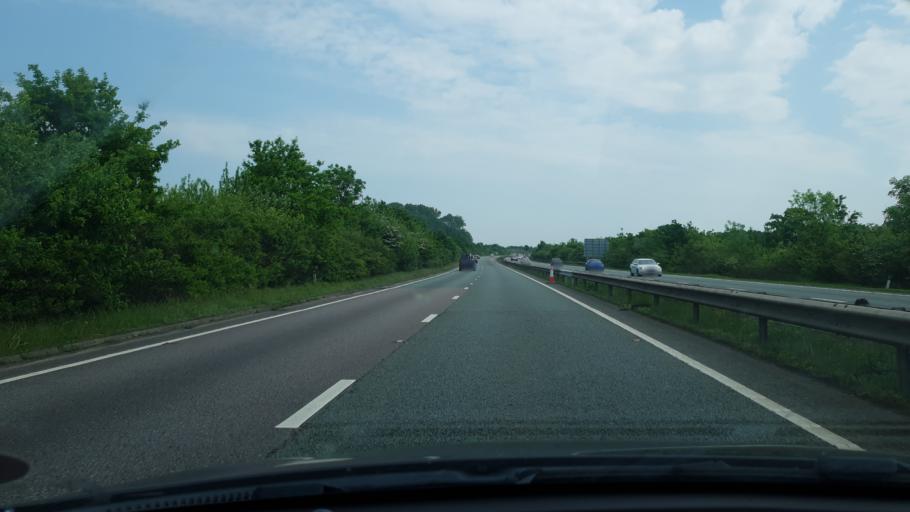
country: GB
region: England
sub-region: Northamptonshire
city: Brixworth
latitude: 52.4028
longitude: -0.8989
